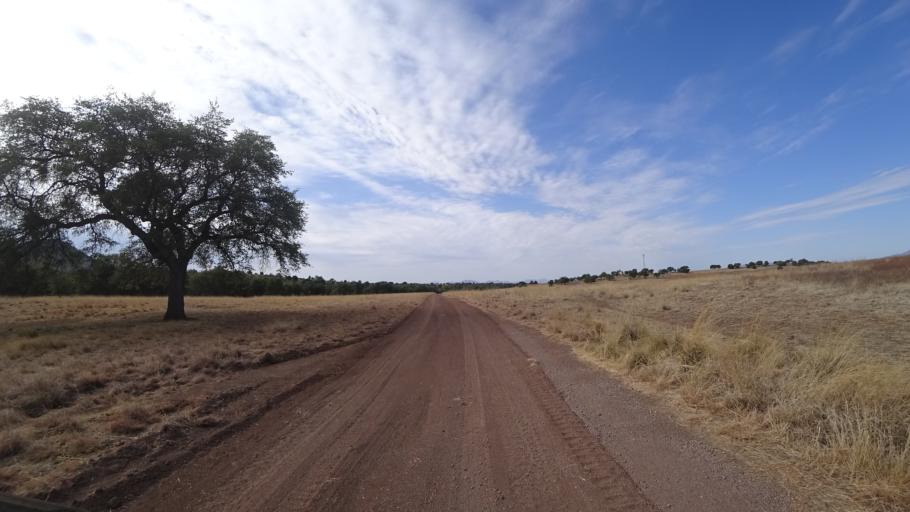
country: MX
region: Sonora
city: Santa Cruz
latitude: 31.4912
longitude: -110.5724
